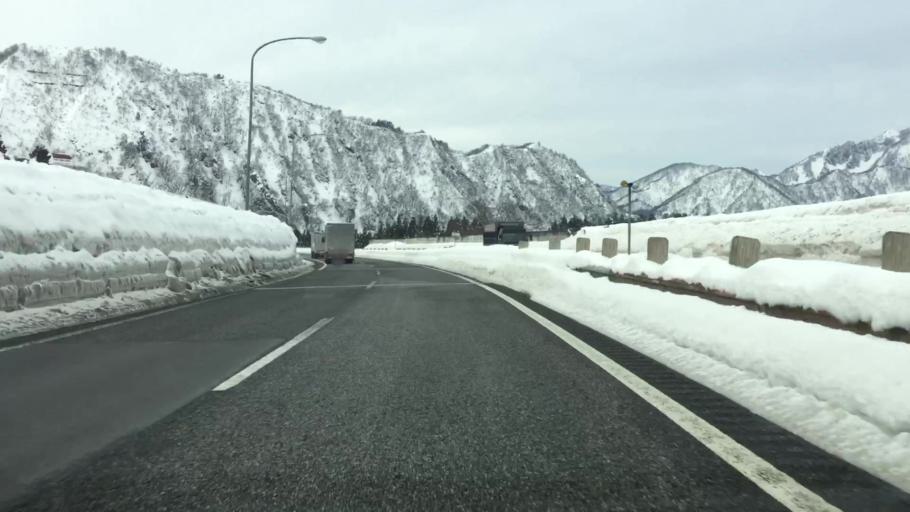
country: JP
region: Niigata
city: Shiozawa
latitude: 36.9056
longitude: 138.8462
